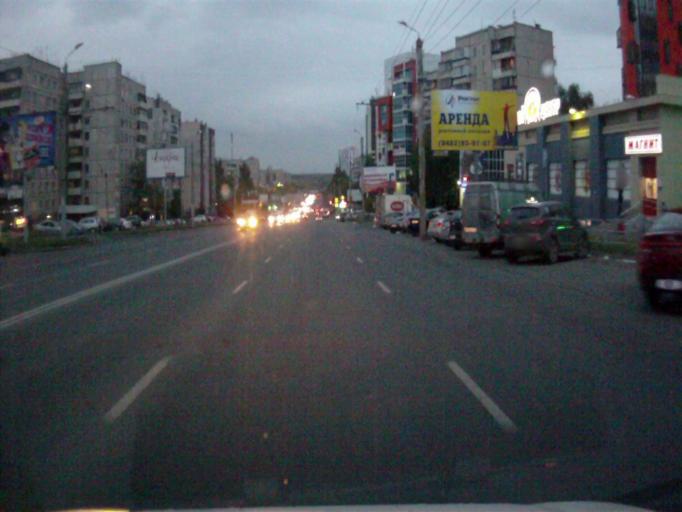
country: RU
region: Chelyabinsk
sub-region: Gorod Chelyabinsk
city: Chelyabinsk
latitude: 55.1858
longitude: 61.3325
